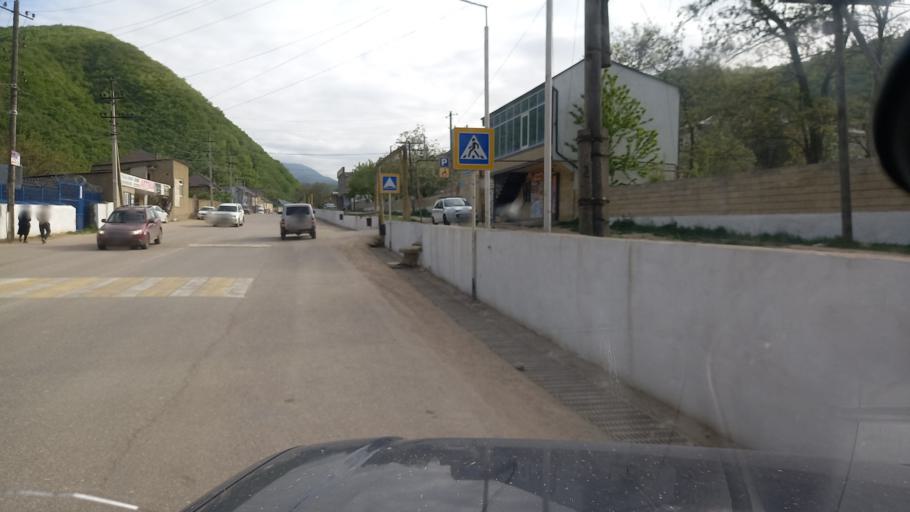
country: RU
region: Dagestan
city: Khuchni
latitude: 41.9611
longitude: 47.9566
